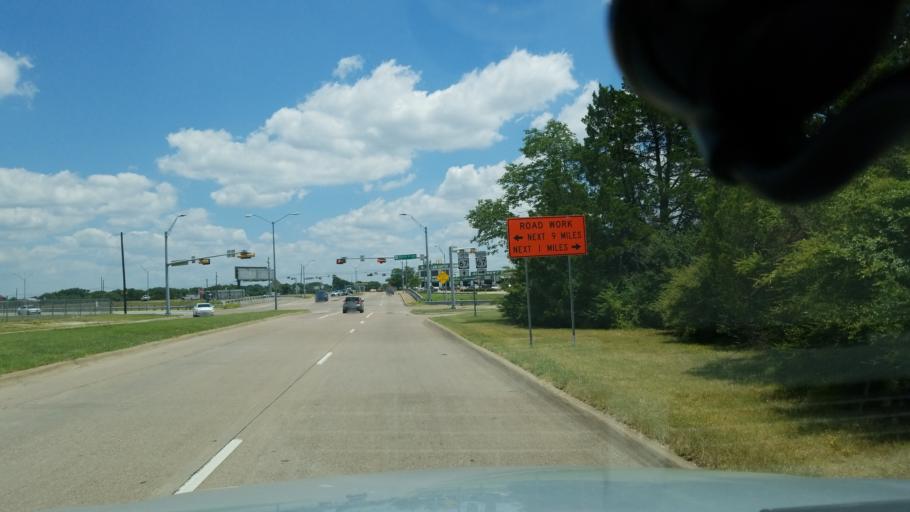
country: US
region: Texas
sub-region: Dallas County
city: Duncanville
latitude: 32.6710
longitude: -96.8634
